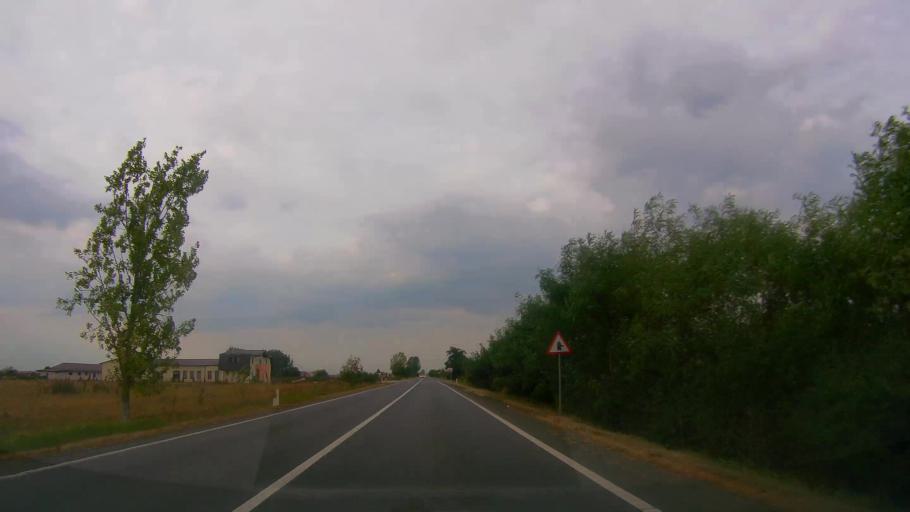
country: RO
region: Satu Mare
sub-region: Comuna Agris
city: Agris
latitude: 47.8594
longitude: 22.9845
